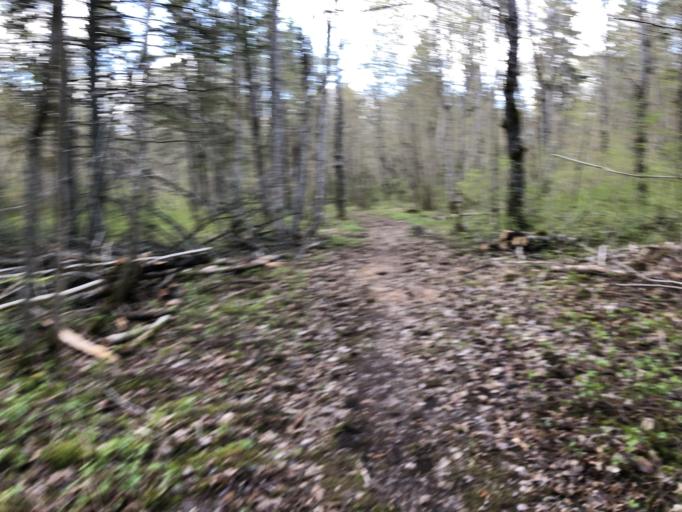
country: EE
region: Harju
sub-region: Harku vald
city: Tabasalu
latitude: 59.4410
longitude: 24.5239
